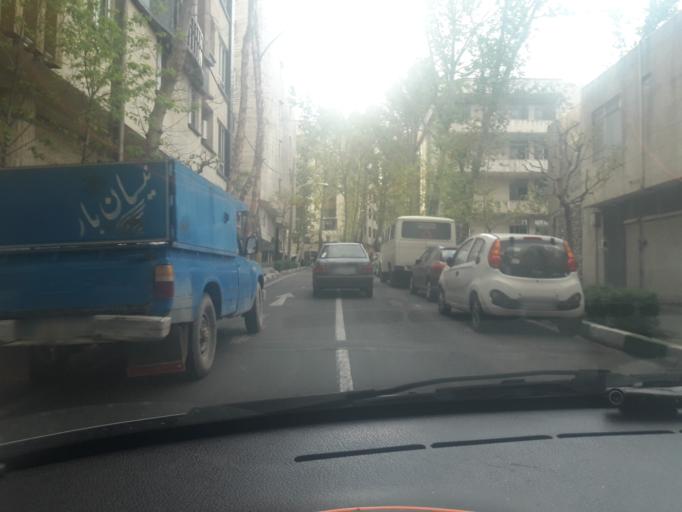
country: IR
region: Tehran
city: Tehran
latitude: 35.7395
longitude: 51.4066
